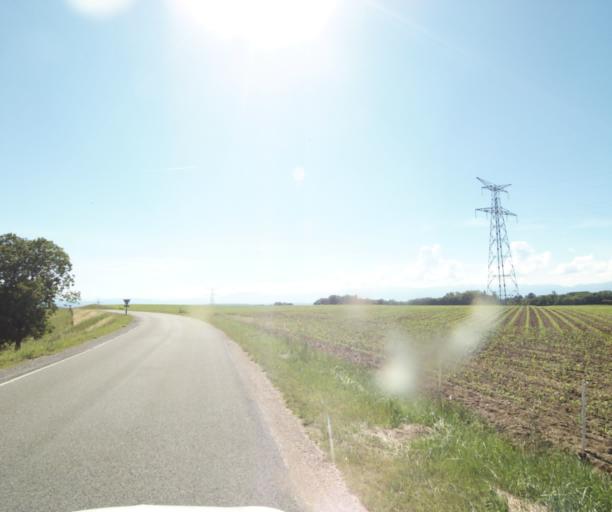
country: FR
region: Rhone-Alpes
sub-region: Departement de la Haute-Savoie
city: Saint-Cergues
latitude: 46.2645
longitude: 6.3332
